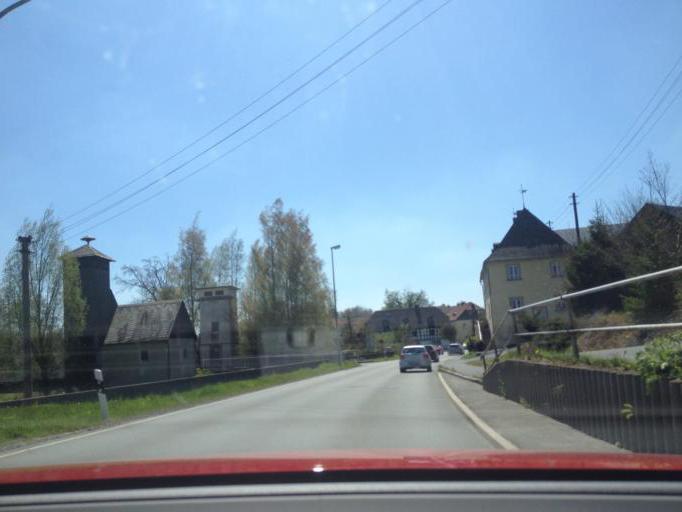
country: DE
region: Bavaria
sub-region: Upper Franconia
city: Oberkotzau
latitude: 50.2453
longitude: 11.9364
